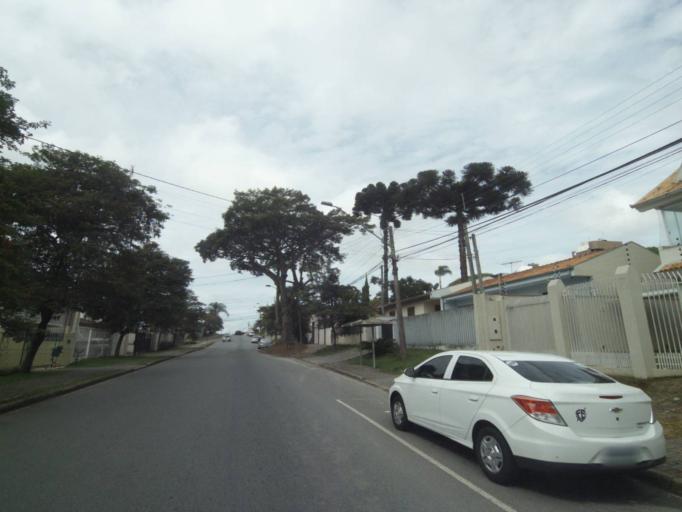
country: BR
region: Parana
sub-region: Curitiba
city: Curitiba
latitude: -25.4364
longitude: -49.3124
